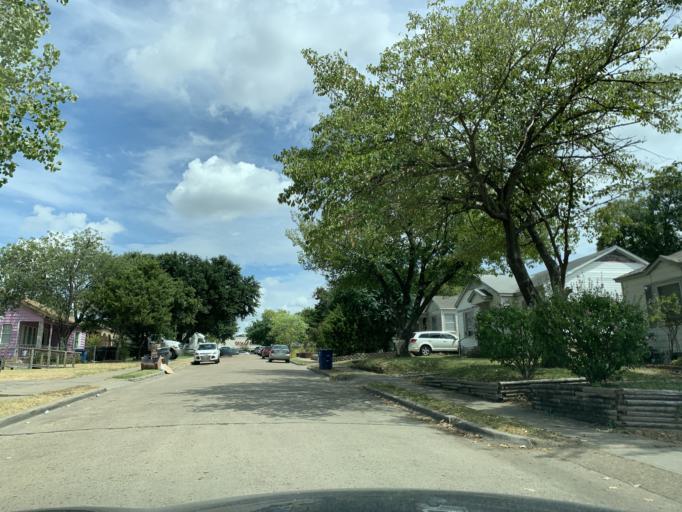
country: US
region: Texas
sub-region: Dallas County
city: Cockrell Hill
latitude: 32.7340
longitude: -96.8760
